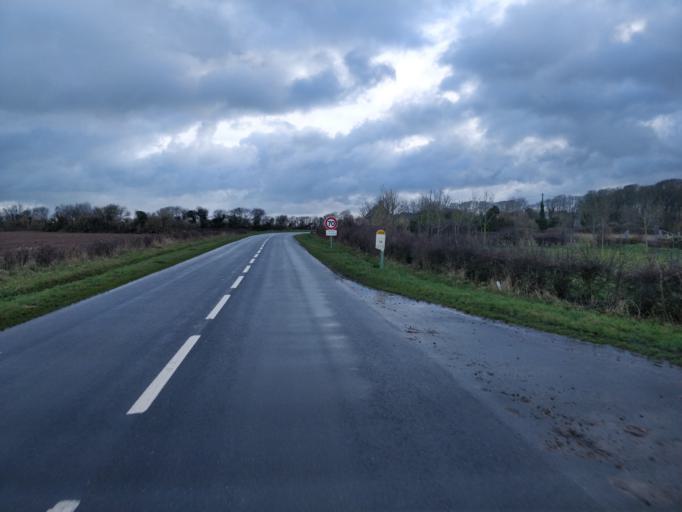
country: FR
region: Lower Normandy
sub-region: Departement du Calvados
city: Grandcamp-Maisy
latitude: 49.3839
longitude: -0.9267
